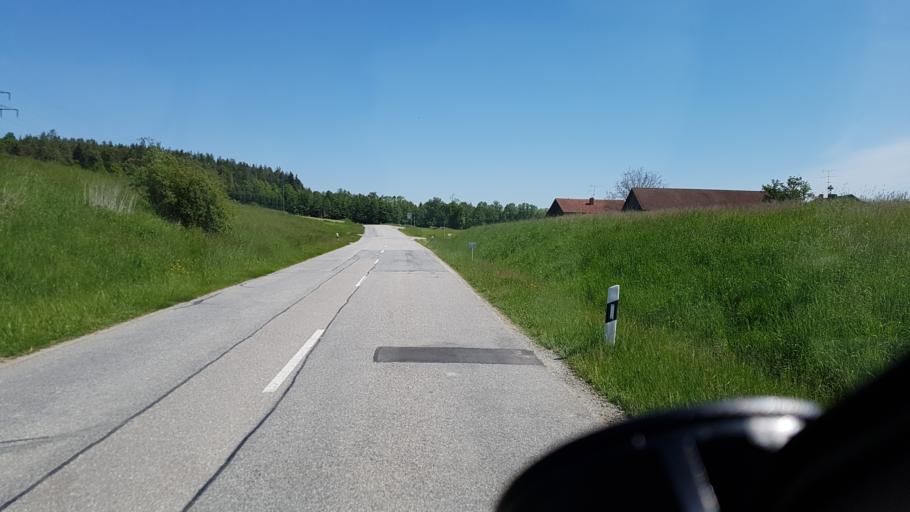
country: DE
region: Bavaria
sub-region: Lower Bavaria
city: Postmunster
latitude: 48.3952
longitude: 12.9245
